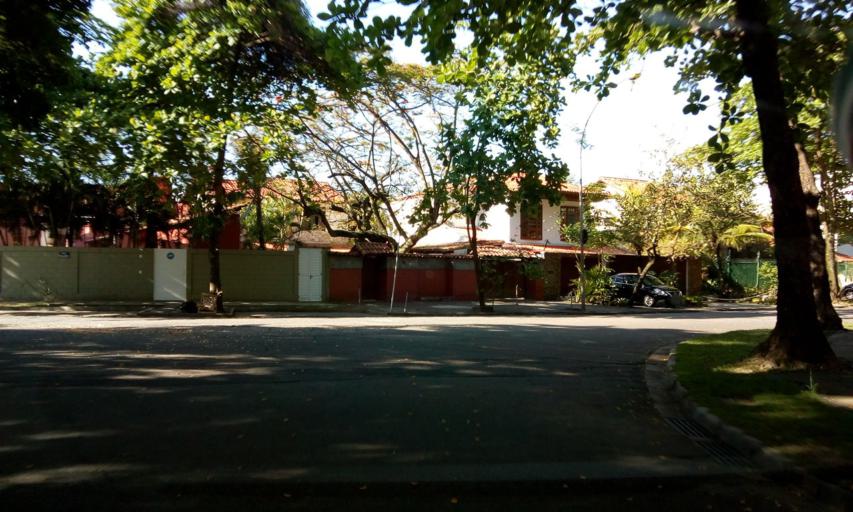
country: BR
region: Rio de Janeiro
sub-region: Nilopolis
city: Nilopolis
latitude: -22.9982
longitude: -43.3790
